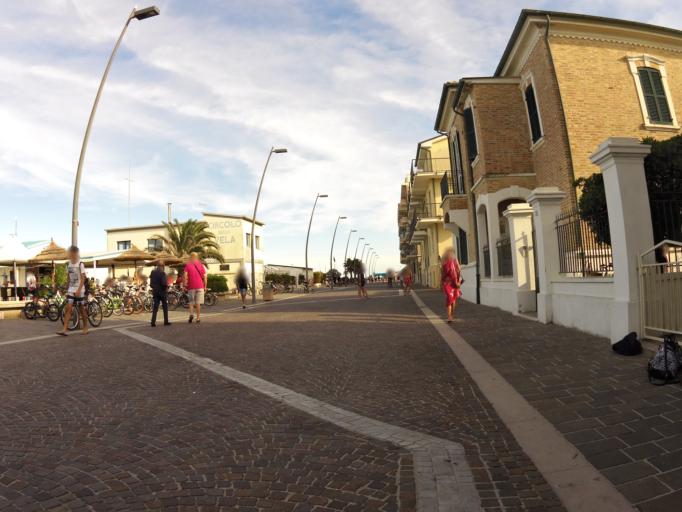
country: IT
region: The Marches
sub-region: Provincia di Macerata
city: Porto Recanati
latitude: 43.4291
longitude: 13.6674
